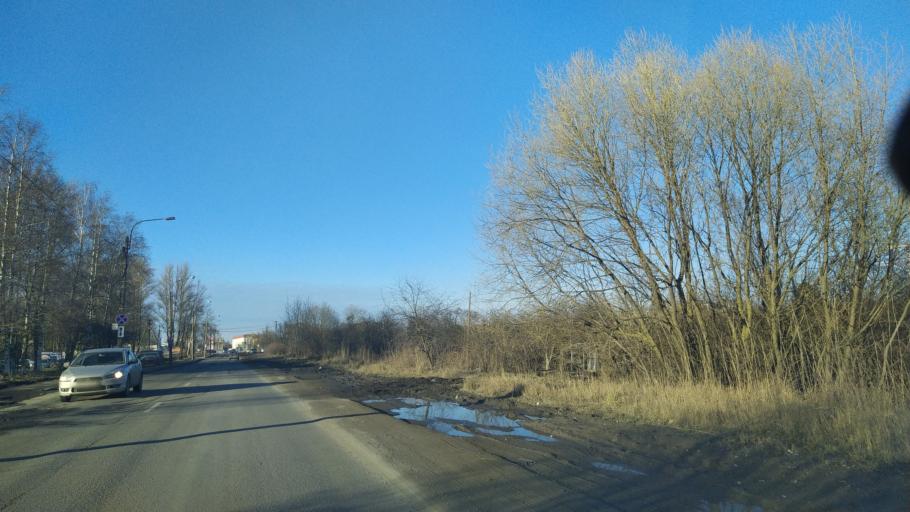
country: RU
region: St.-Petersburg
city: Pushkin
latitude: 59.6963
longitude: 30.3954
